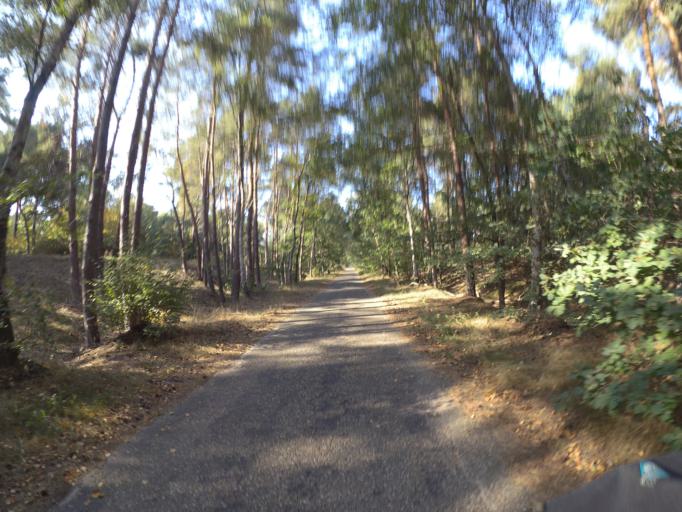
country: NL
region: North Brabant
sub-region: Gemeente Oirschot
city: Oirschot
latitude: 51.4709
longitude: 5.3318
